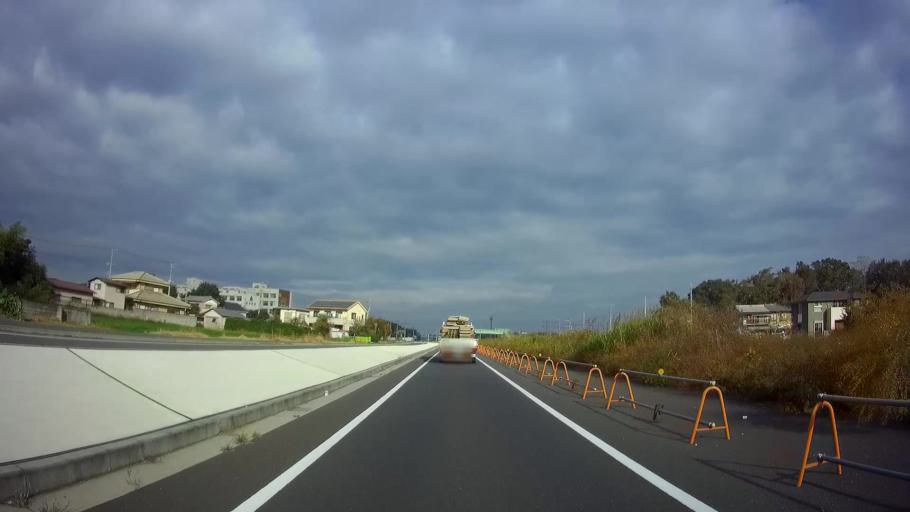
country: JP
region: Saitama
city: Okegawa
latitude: 35.9830
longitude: 139.5342
